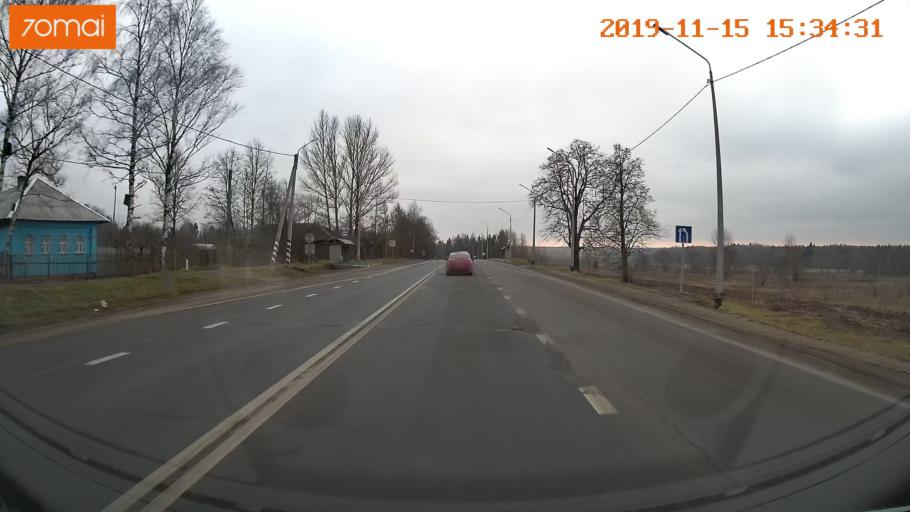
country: RU
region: Jaroslavl
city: Danilov
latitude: 58.0685
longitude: 40.0887
